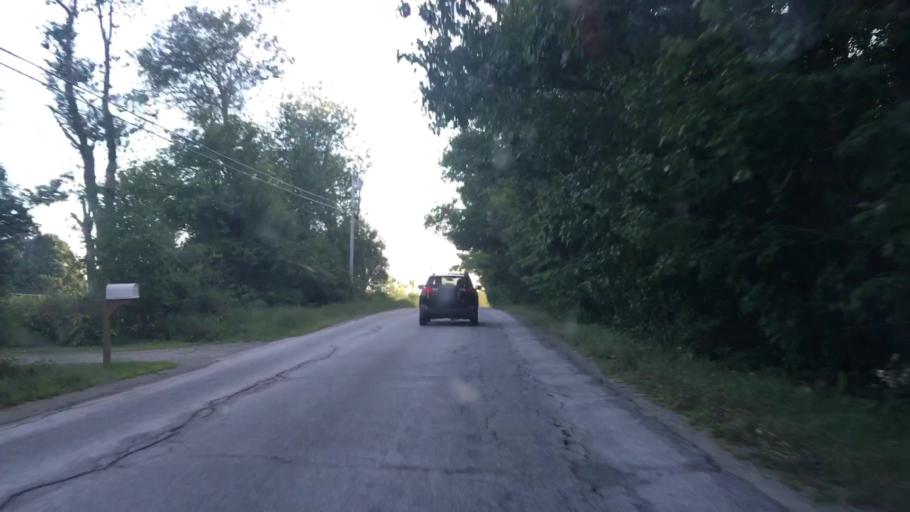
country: US
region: Maine
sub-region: Waldo County
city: Frankfort
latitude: 44.6783
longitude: -68.9155
